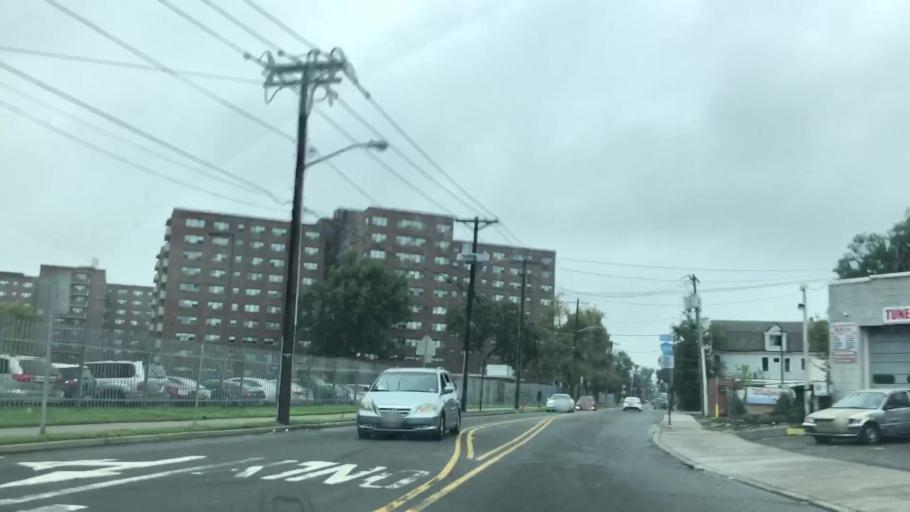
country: US
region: New Jersey
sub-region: Essex County
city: Irvington
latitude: 40.7285
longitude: -74.2205
